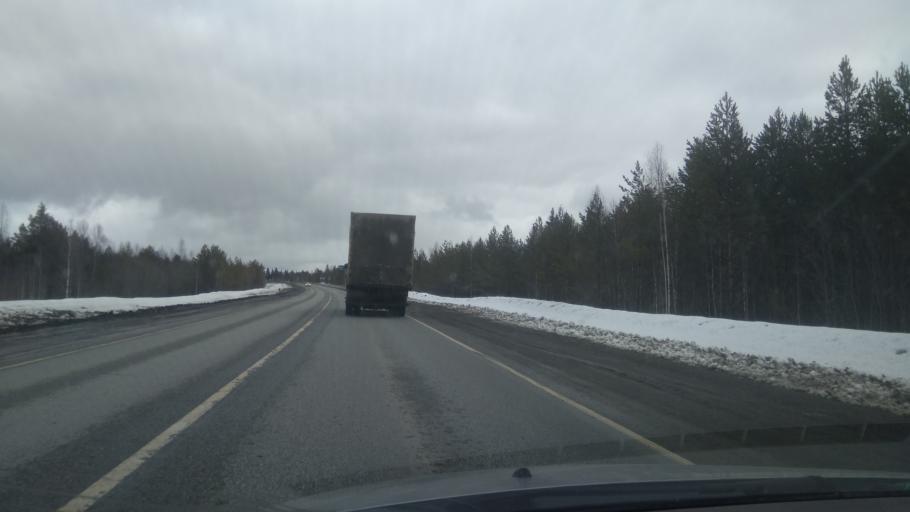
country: RU
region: Sverdlovsk
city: Atig
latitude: 56.7968
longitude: 59.3975
